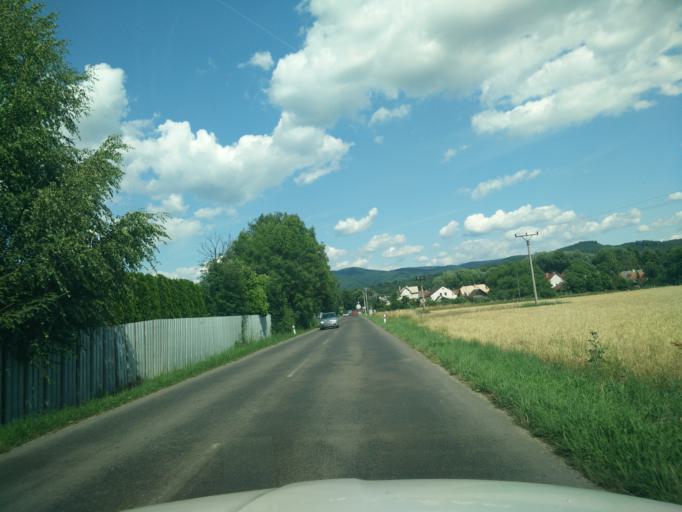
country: SK
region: Nitriansky
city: Prievidza
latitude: 48.8177
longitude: 18.6384
